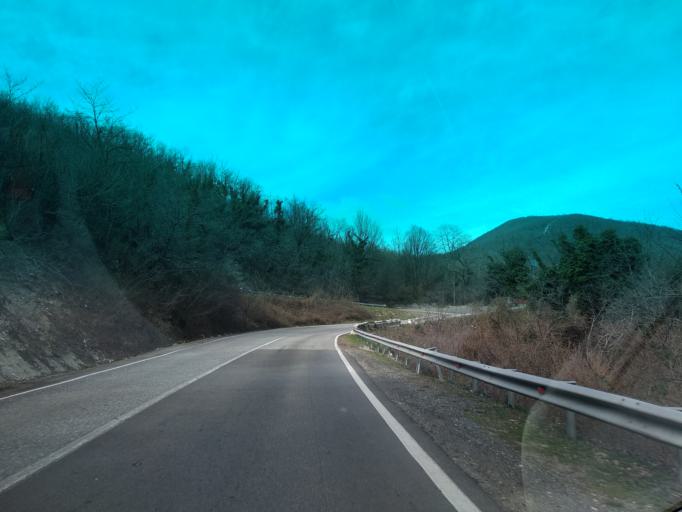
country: RU
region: Krasnodarskiy
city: Shepsi
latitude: 44.0723
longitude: 39.1402
